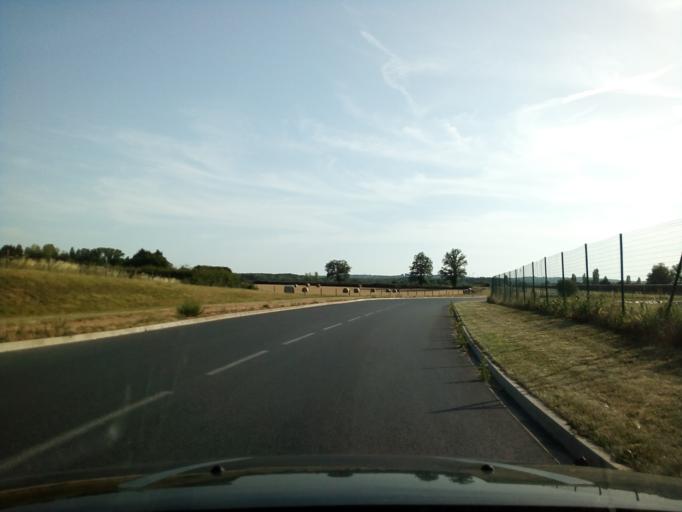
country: FR
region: Auvergne
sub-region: Departement de l'Allier
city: Domerat
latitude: 46.3633
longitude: 2.5569
